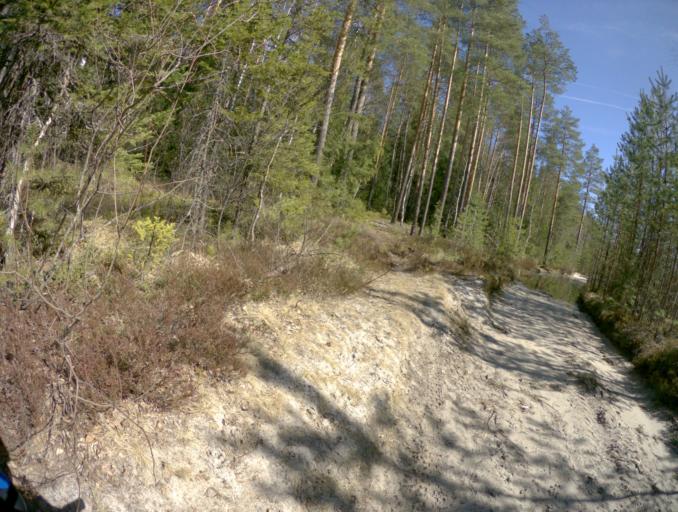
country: RU
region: Vladimir
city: Ivanishchi
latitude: 55.8037
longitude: 40.4210
